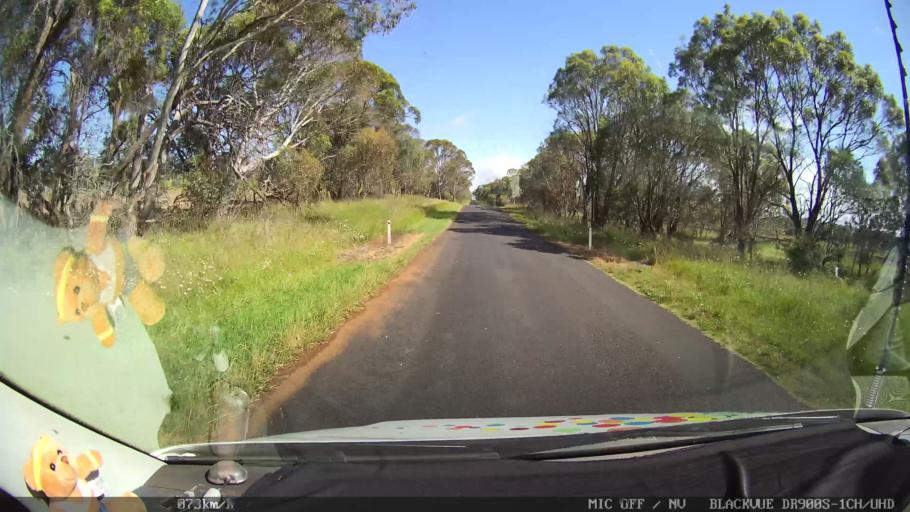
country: AU
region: New South Wales
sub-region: Guyra
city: Guyra
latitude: -30.0941
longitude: 151.6788
